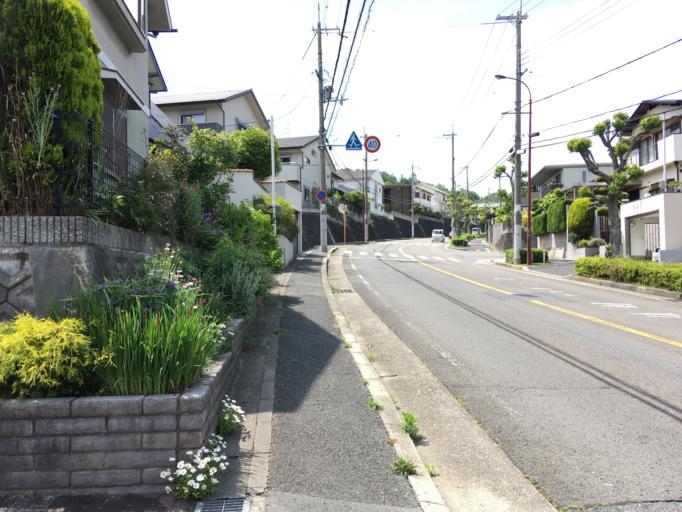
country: JP
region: Nara
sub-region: Ikoma-shi
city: Ikoma
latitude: 34.7123
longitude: 135.7160
